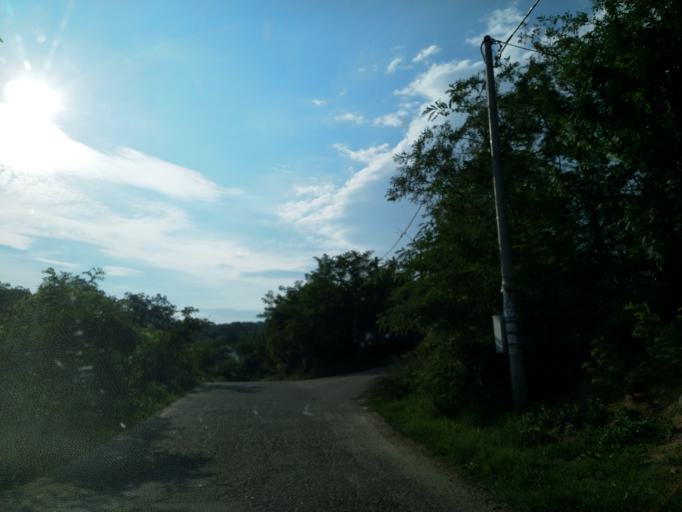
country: RS
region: Central Serbia
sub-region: Pomoravski Okrug
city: Jagodina
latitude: 44.0062
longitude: 21.1792
